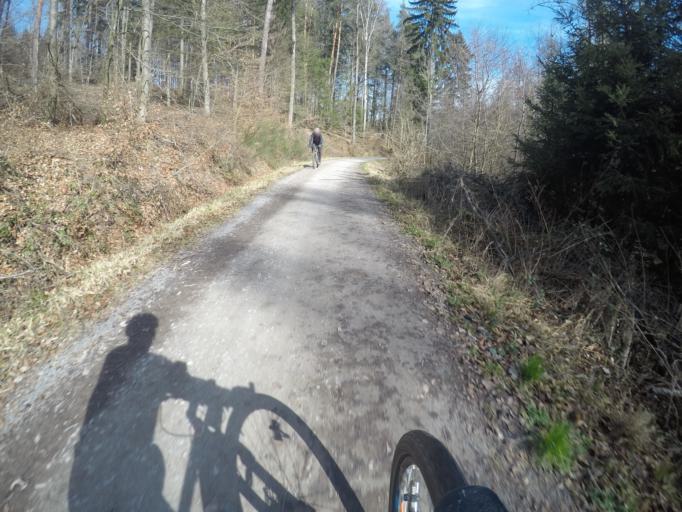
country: DE
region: Baden-Wuerttemberg
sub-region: Regierungsbezirk Stuttgart
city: Gerlingen
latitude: 48.7844
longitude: 9.0978
